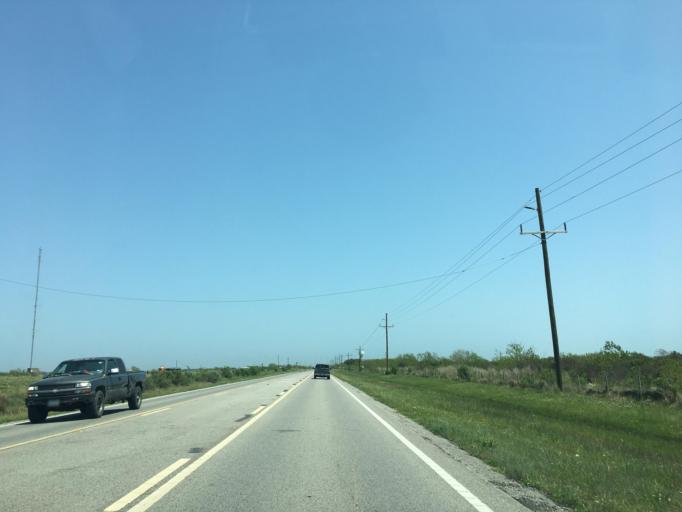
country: US
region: Texas
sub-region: Galveston County
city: Galveston
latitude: 29.4109
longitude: -94.7148
